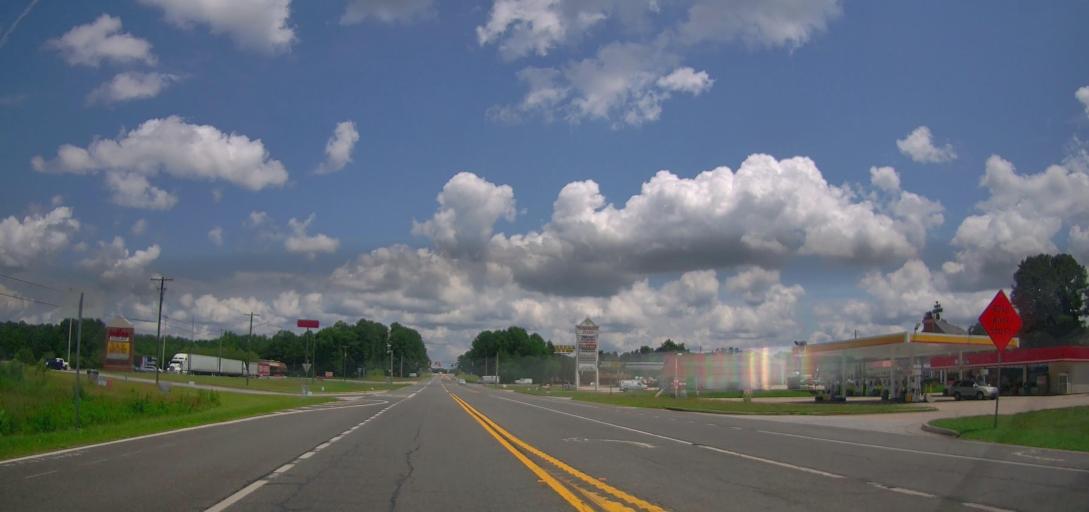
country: US
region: Georgia
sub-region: Troup County
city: Hogansville
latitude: 33.1615
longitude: -84.8741
